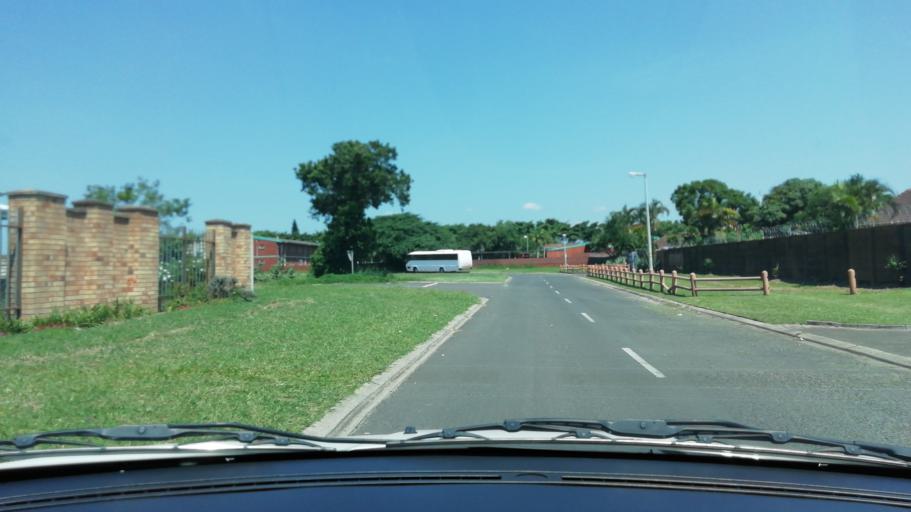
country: ZA
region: KwaZulu-Natal
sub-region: uThungulu District Municipality
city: Richards Bay
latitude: -28.7395
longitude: 32.0559
